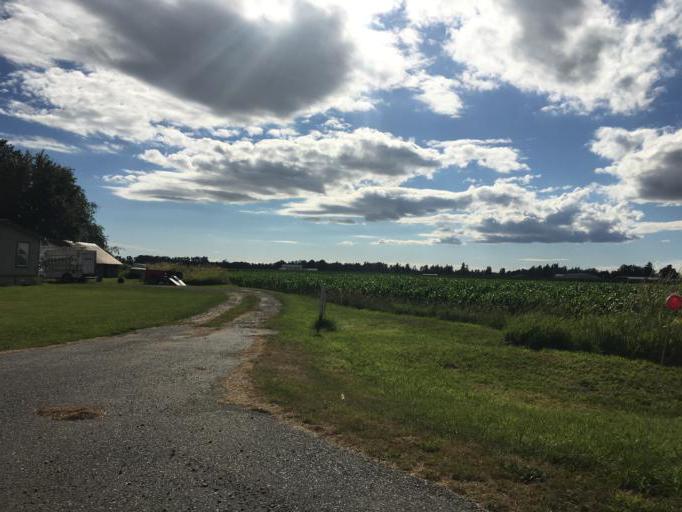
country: US
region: Washington
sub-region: Whatcom County
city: Nooksack
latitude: 48.9609
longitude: -122.3093
